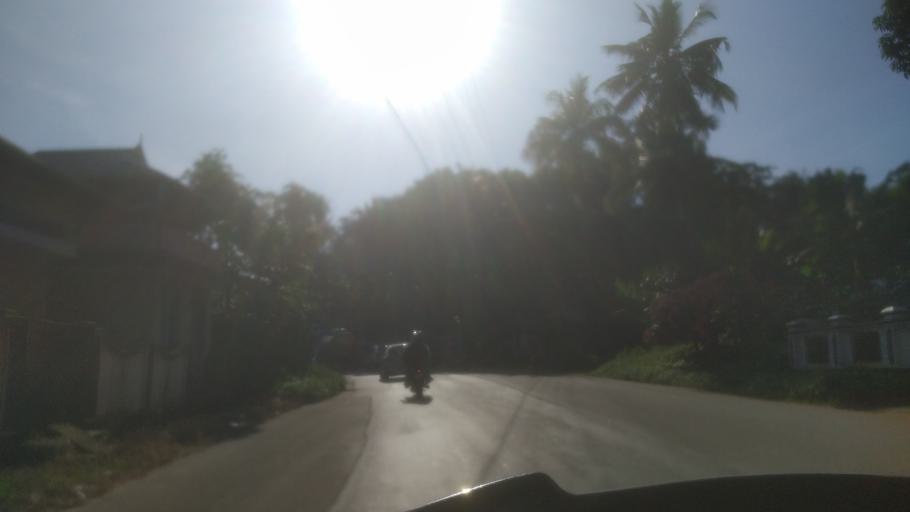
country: IN
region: Kerala
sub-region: Ernakulam
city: Ramamangalam
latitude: 9.9800
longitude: 76.5165
